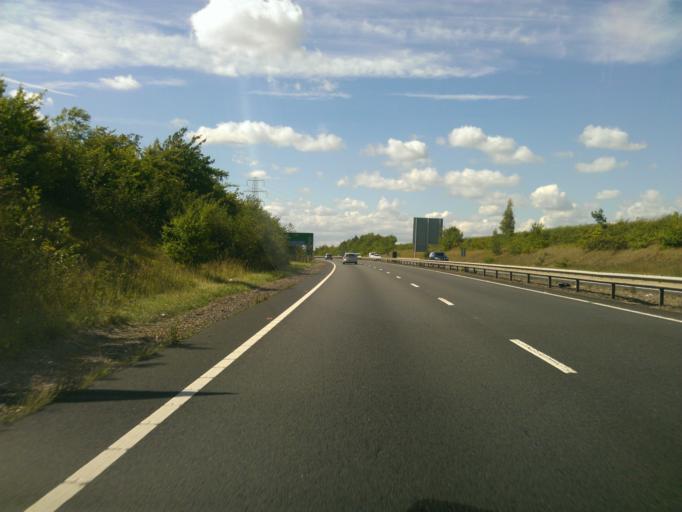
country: GB
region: England
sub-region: Northamptonshire
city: Raunds
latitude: 52.3734
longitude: -0.4621
